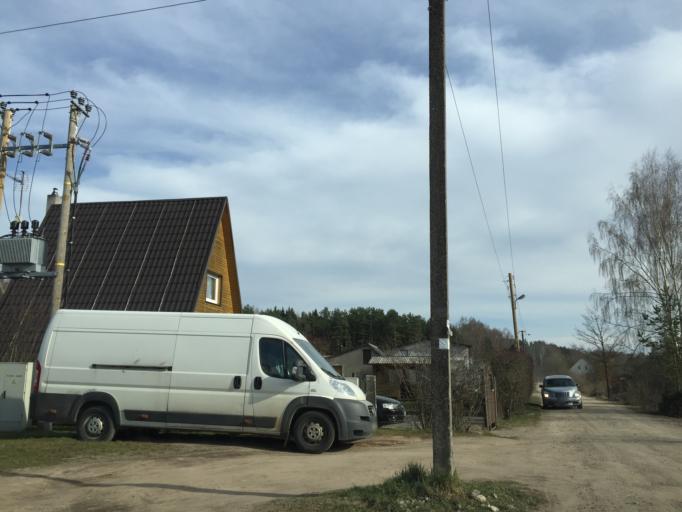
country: LV
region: Ogre
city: Ogre
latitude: 56.8063
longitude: 24.6401
